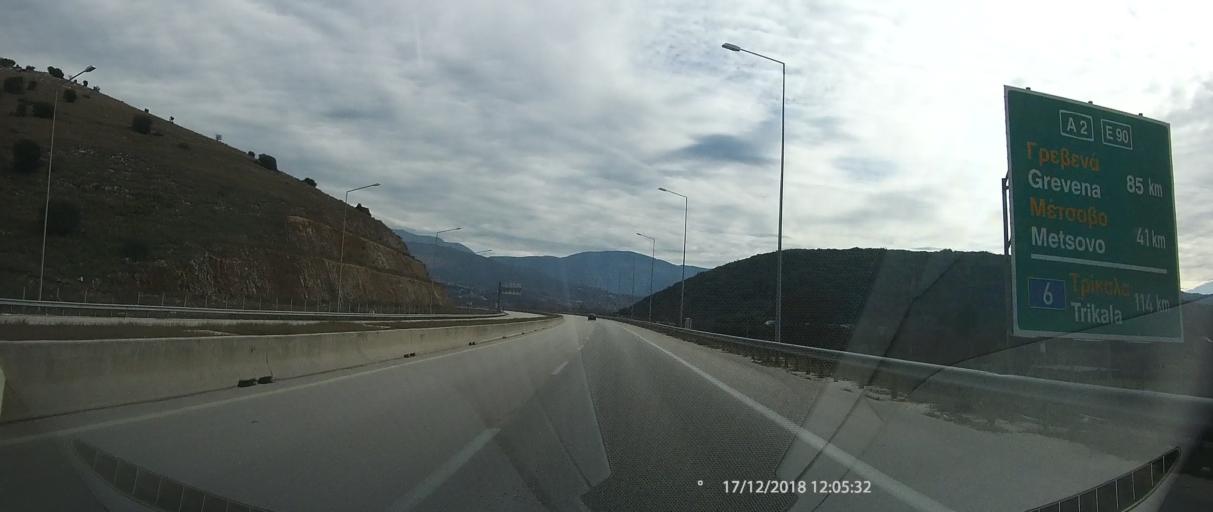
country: GR
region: Epirus
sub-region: Nomos Ioanninon
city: Koutselio
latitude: 39.5983
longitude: 20.9135
